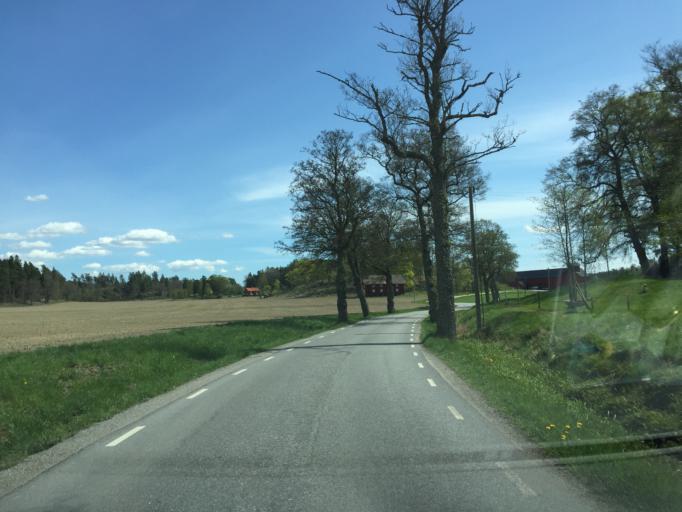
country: SE
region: Stockholm
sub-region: Sodertalje Kommun
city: Soedertaelje
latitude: 59.2481
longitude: 17.6655
